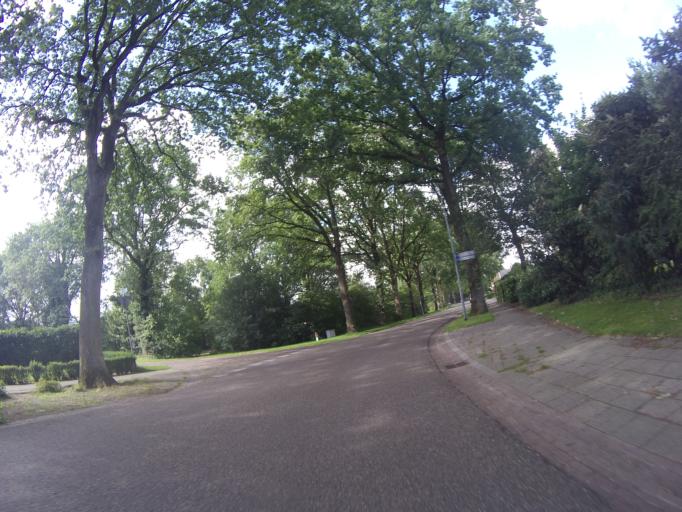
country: NL
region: Drenthe
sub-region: Gemeente Coevorden
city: Dalen
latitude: 52.7535
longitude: 6.7187
